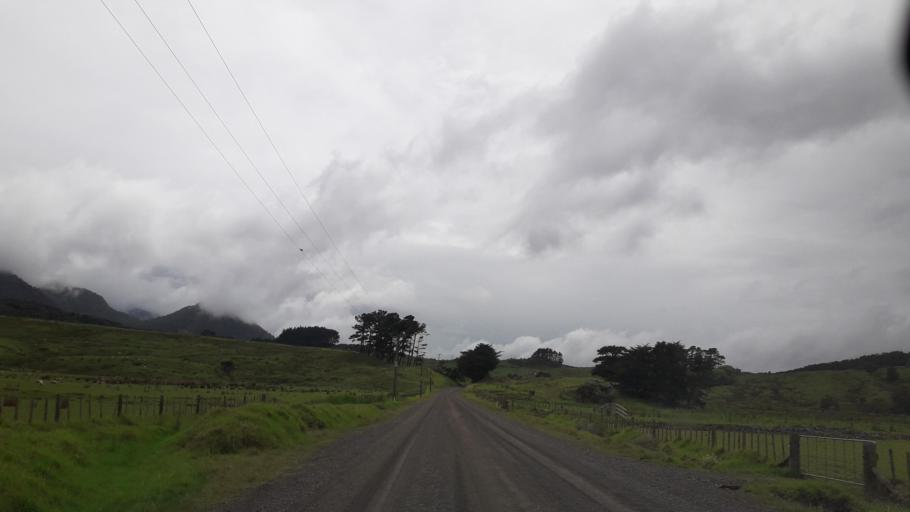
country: NZ
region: Northland
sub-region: Far North District
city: Ahipara
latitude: -35.4220
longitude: 173.3601
